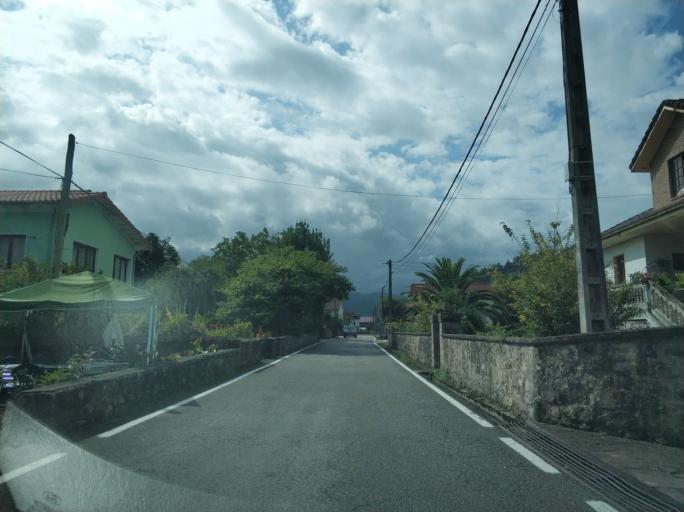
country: ES
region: Cantabria
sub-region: Provincia de Cantabria
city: Polanco
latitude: 43.3701
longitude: -3.9694
